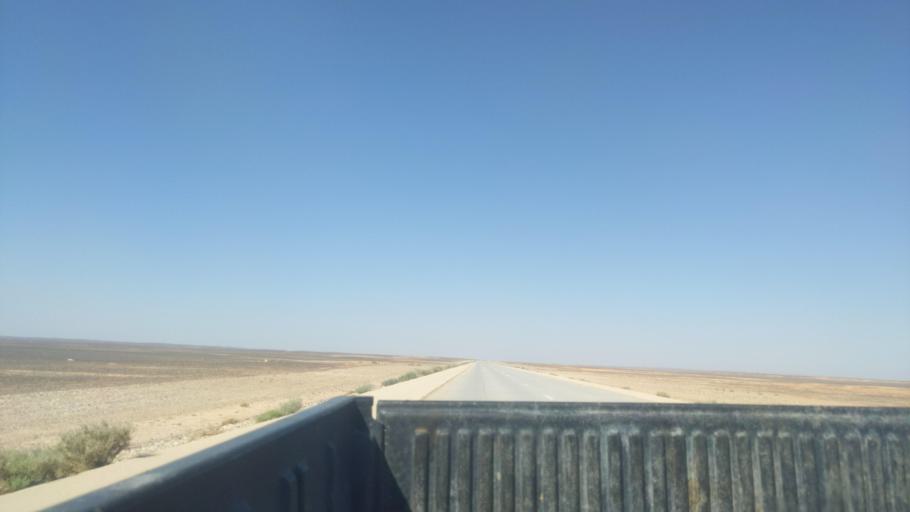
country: JO
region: Amman
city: Al Azraq ash Shamali
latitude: 31.4601
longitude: 36.7945
